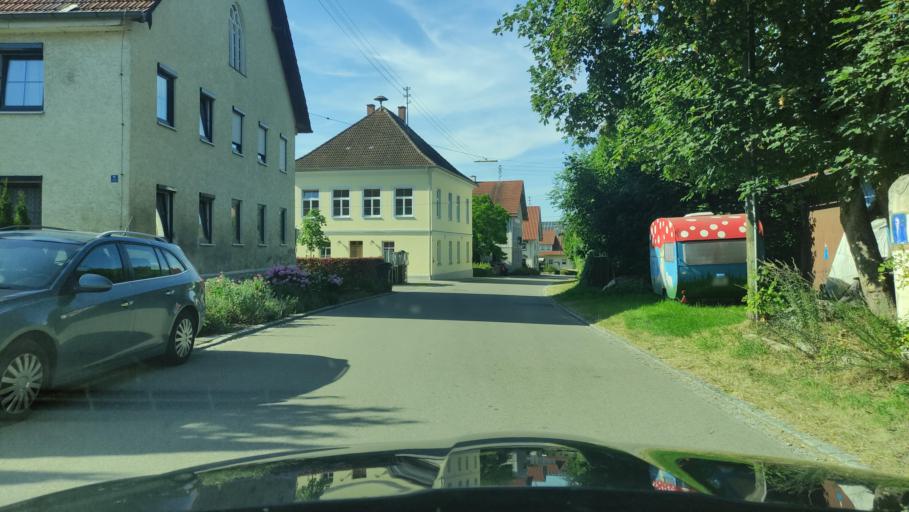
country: DE
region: Bavaria
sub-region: Swabia
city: Ebershausen
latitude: 48.2109
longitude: 10.2863
